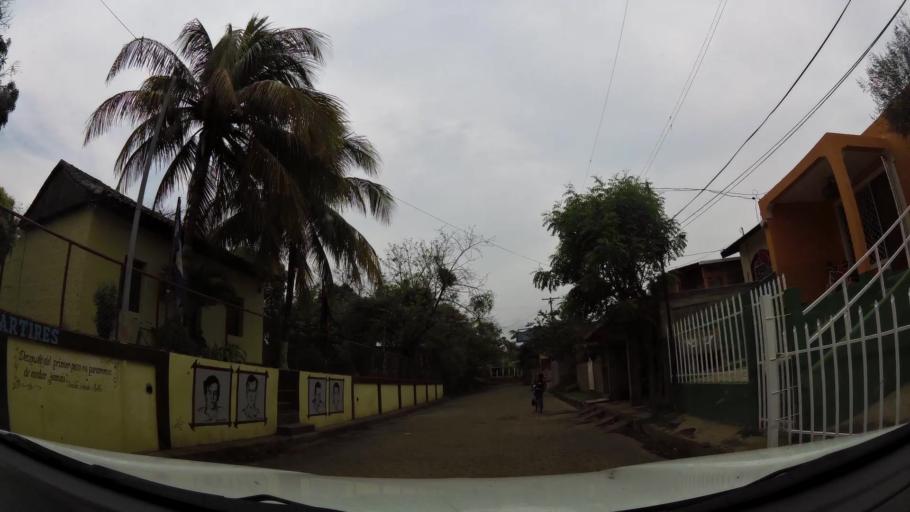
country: NI
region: Granada
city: Nandaime
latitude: 11.7569
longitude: -86.0573
